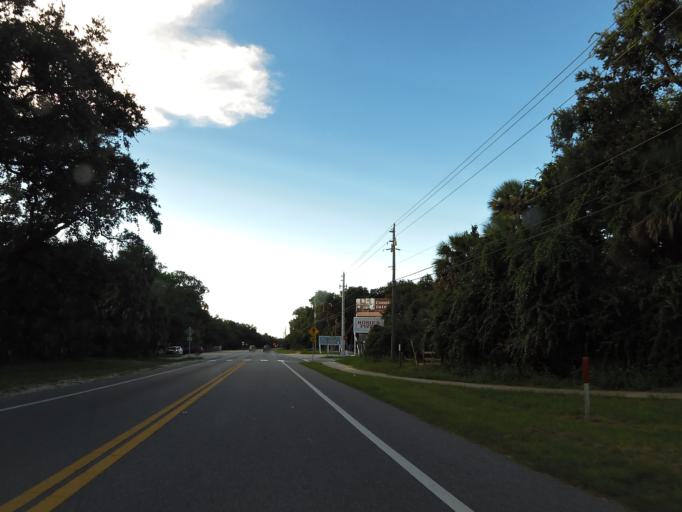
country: US
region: Florida
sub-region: Flagler County
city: Palm Coast
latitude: 29.6146
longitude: -81.2025
